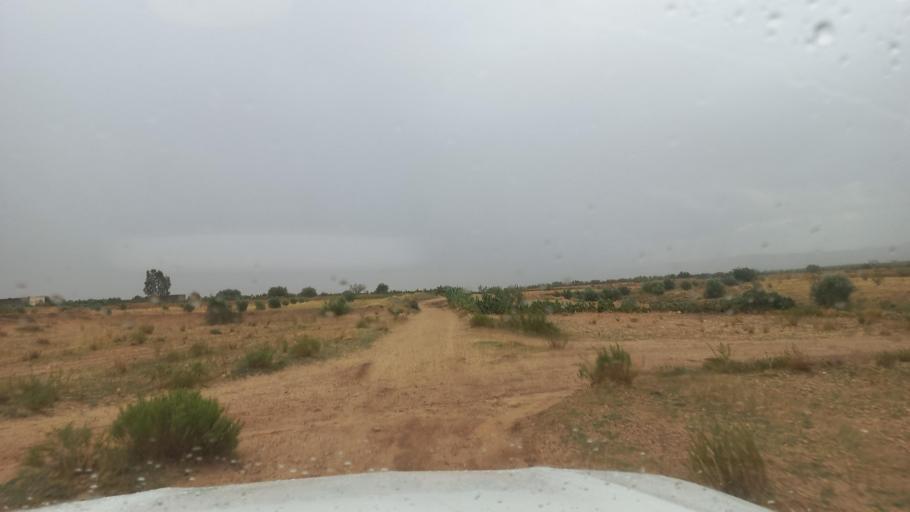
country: TN
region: Al Qasrayn
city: Kasserine
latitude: 35.2687
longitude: 8.9474
